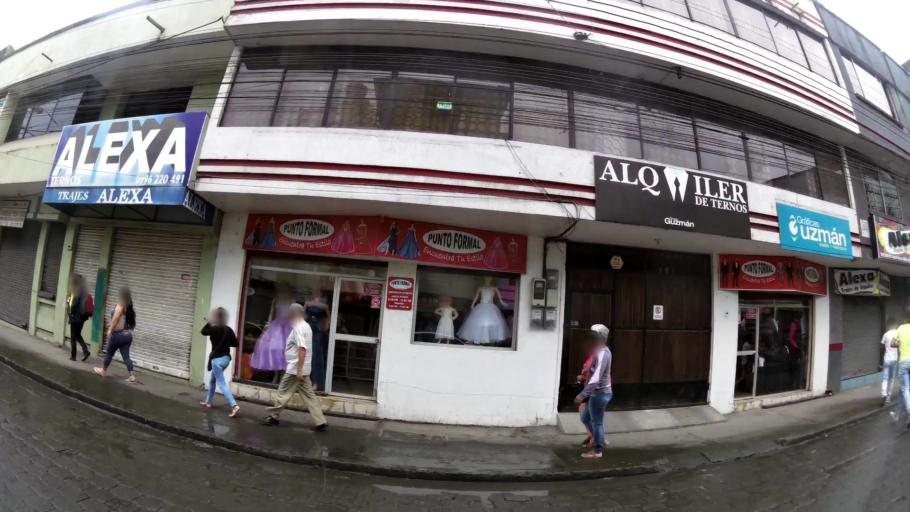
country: EC
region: Santo Domingo de los Tsachilas
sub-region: Canton Santo Domingo de los Colorados
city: Santo Domingo de los Colorados
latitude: -0.2557
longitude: -79.1725
